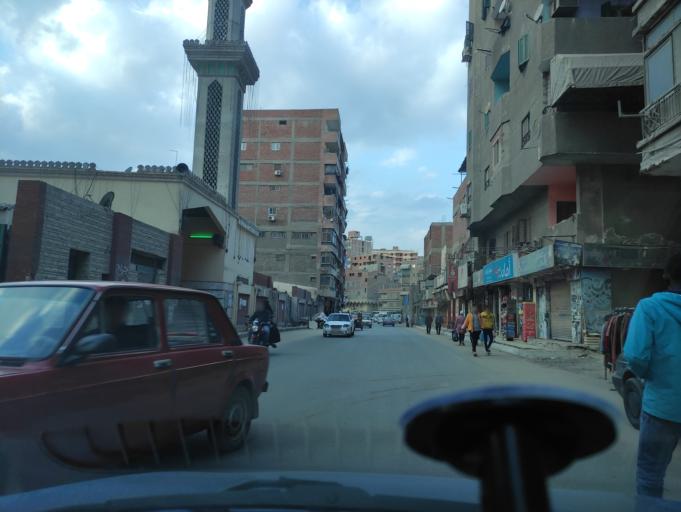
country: EG
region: Muhafazat al Qalyubiyah
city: Al Khankah
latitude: 30.1311
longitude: 31.3609
